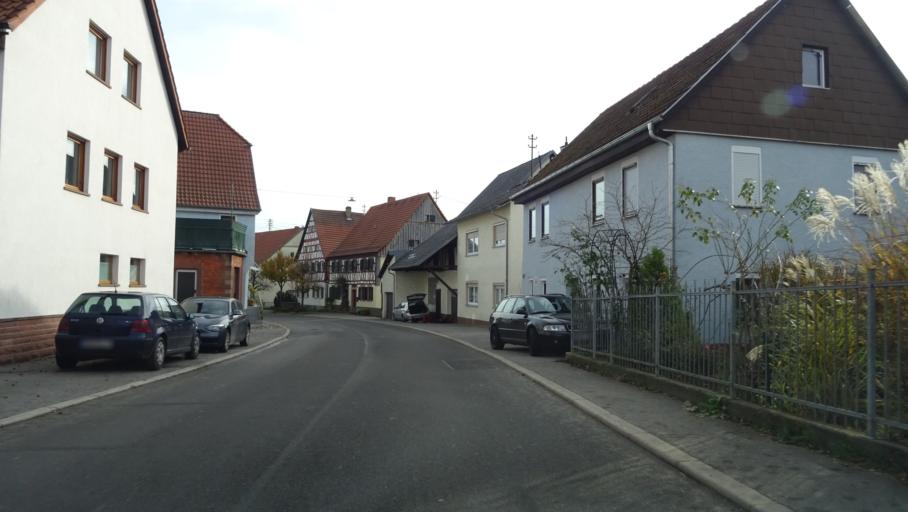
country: DE
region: Baden-Wuerttemberg
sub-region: Karlsruhe Region
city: Fahrenbach
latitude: 49.4007
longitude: 9.1349
